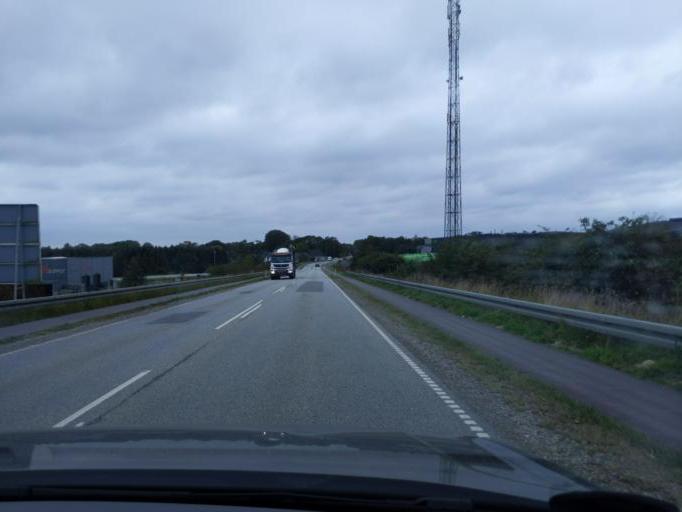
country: DK
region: North Denmark
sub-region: Mariagerfjord Kommune
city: Hobro
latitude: 56.5892
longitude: 9.7697
